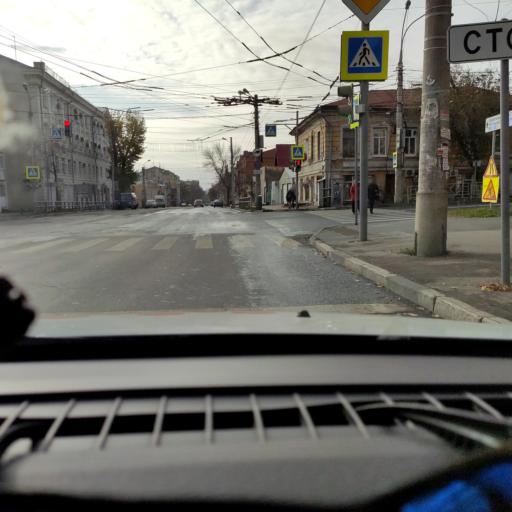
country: RU
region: Samara
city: Samara
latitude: 53.1879
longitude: 50.1019
